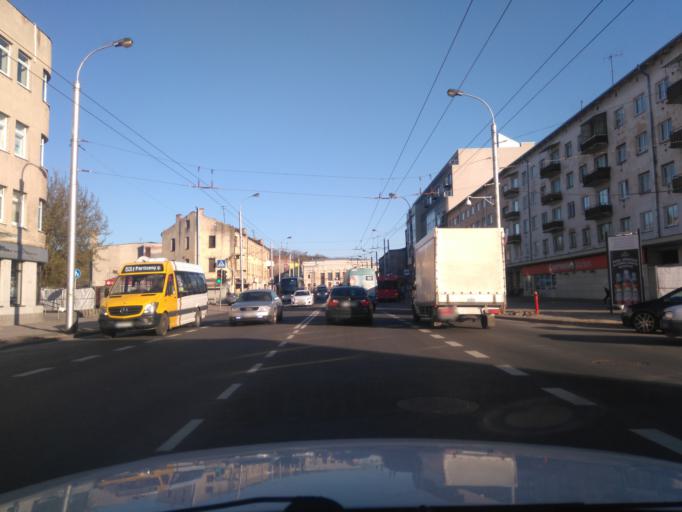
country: LT
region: Kauno apskritis
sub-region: Kaunas
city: Aleksotas
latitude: 54.8884
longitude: 23.9283
